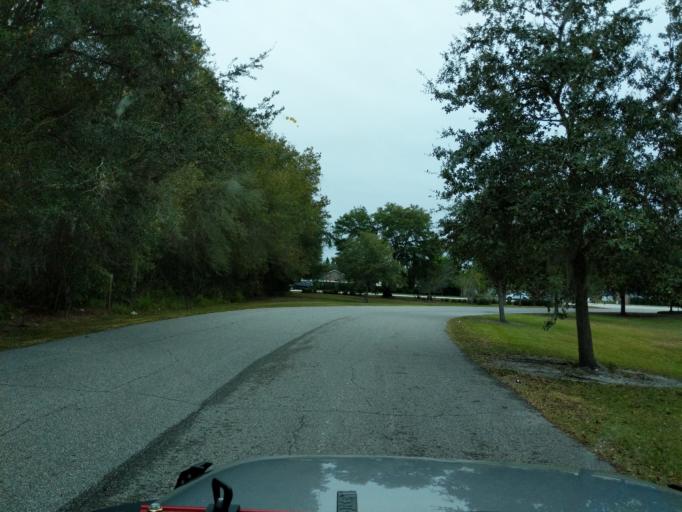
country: US
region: Florida
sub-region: Orange County
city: Winter Garden
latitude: 28.5473
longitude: -81.5845
